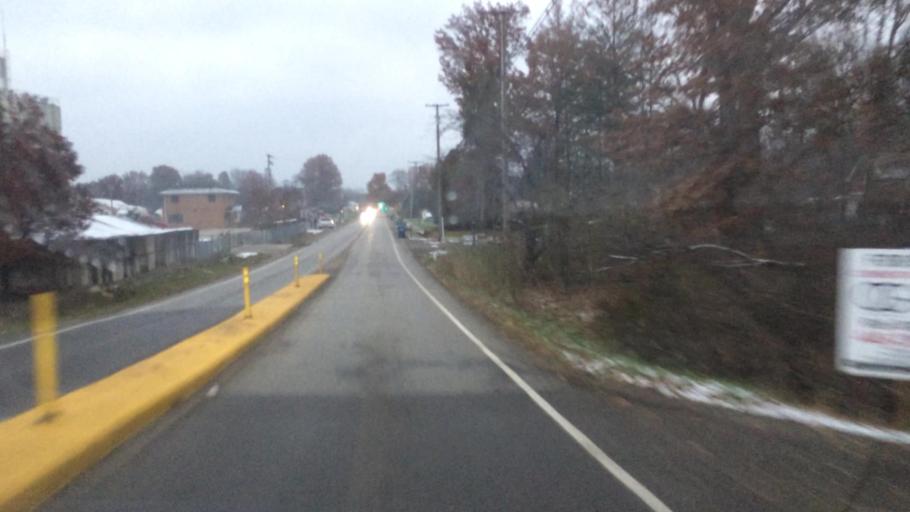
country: US
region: Ohio
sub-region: Cuyahoga County
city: Olmsted Falls
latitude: 41.3508
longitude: -81.9122
